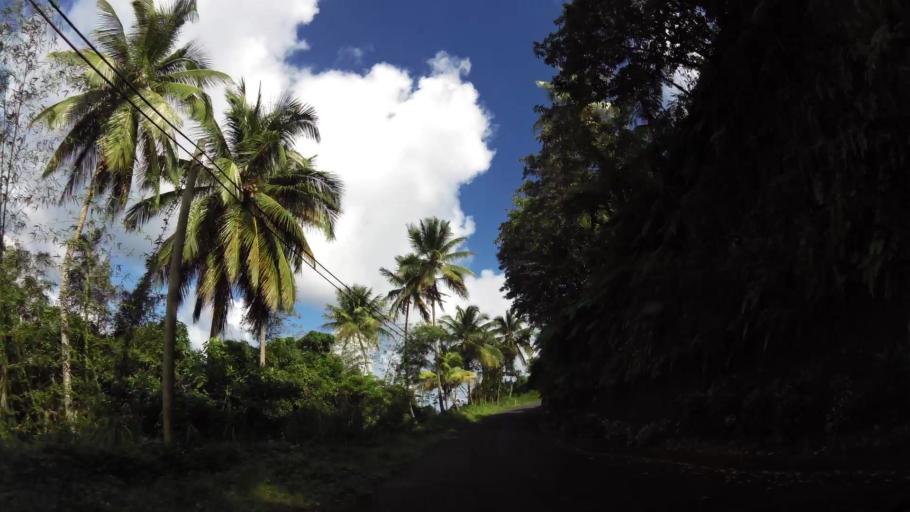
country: DM
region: Saint John
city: Portsmouth
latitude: 15.6180
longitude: -61.4143
